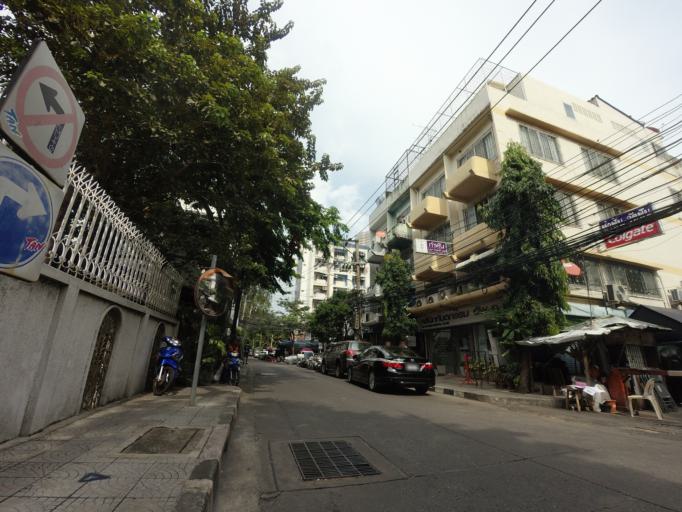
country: TH
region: Bangkok
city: Phaya Thai
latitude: 13.7813
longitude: 100.5436
